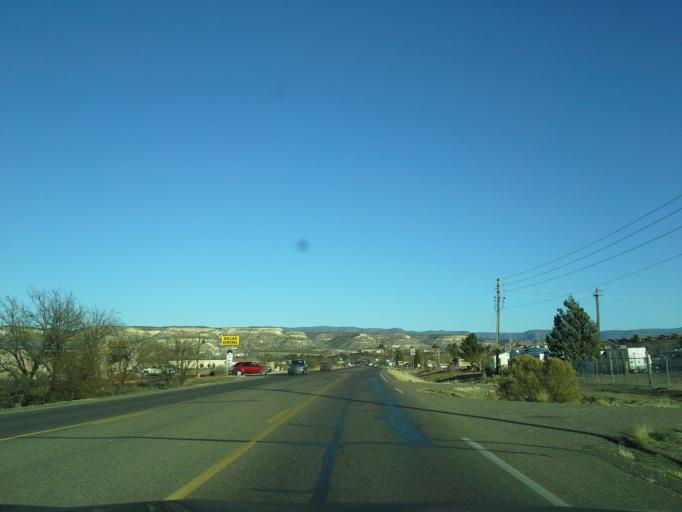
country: US
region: Arizona
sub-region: Yavapai County
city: Camp Verde
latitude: 34.5656
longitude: -111.8725
